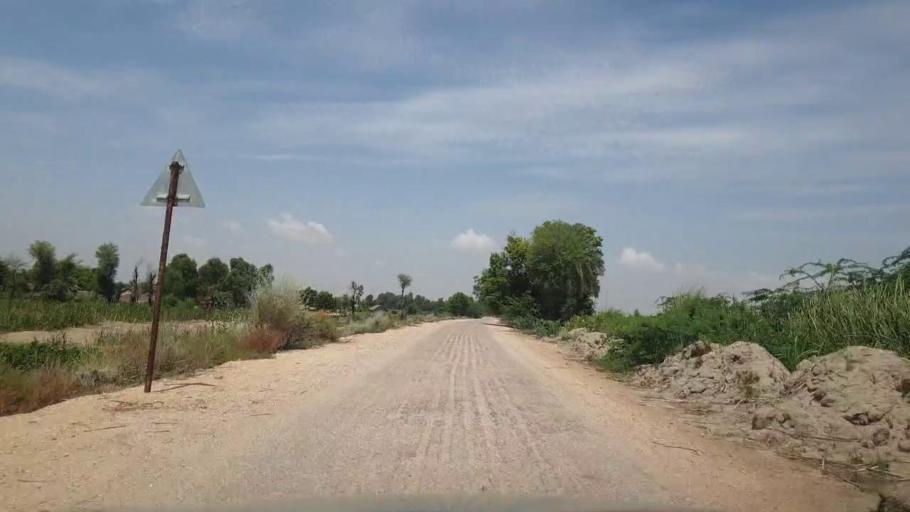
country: PK
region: Sindh
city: Bozdar
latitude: 27.0827
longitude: 68.9785
